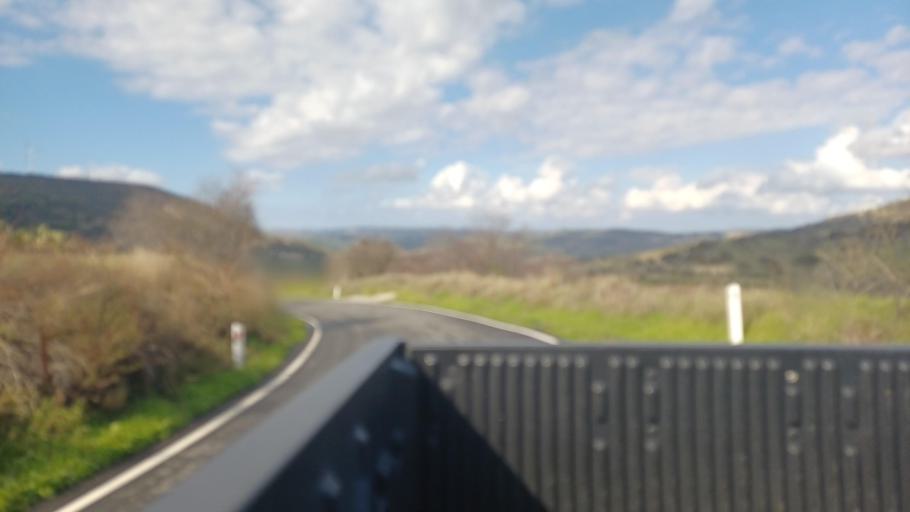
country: CY
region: Limassol
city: Pissouri
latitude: 34.7475
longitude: 32.6716
